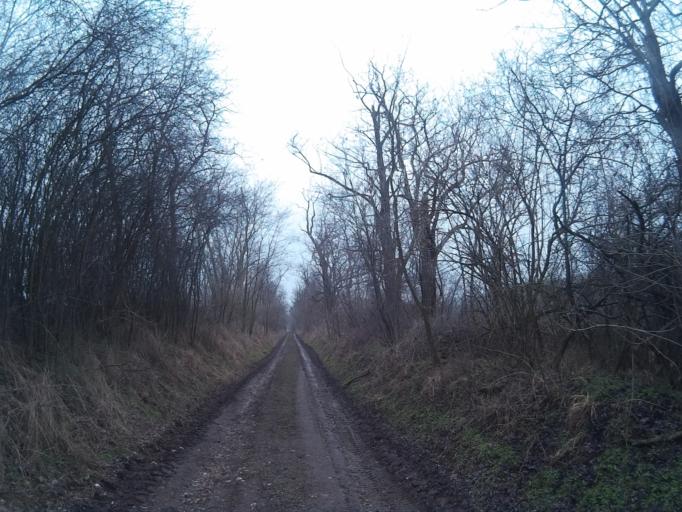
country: HU
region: Komarom-Esztergom
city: Tarjan
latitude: 47.5536
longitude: 18.5600
